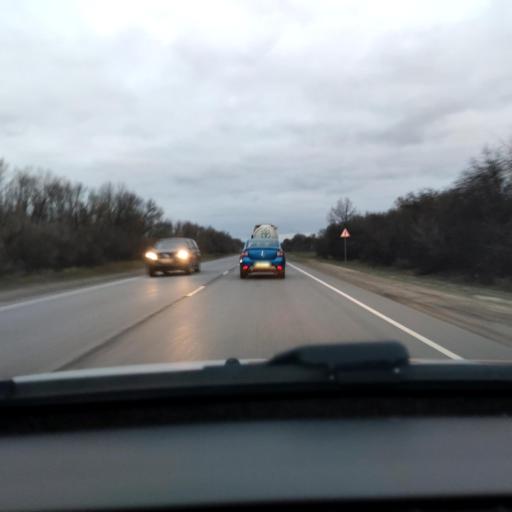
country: RU
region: Lipetsk
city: Borinskoye
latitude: 52.4468
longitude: 39.2898
